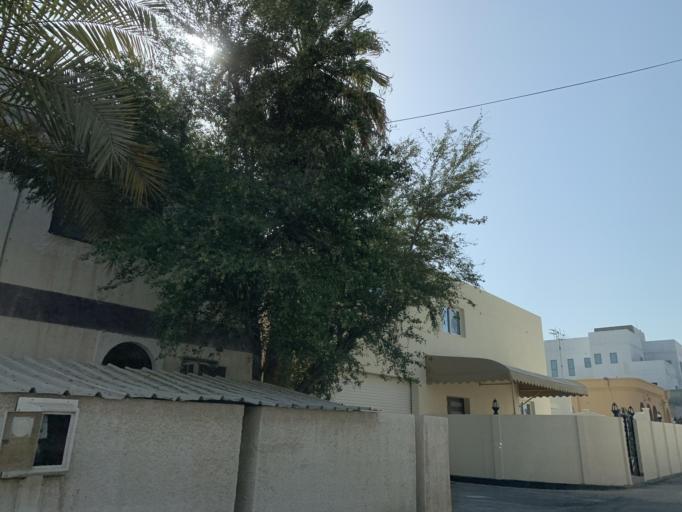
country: BH
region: Muharraq
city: Al Muharraq
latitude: 26.2654
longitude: 50.6145
